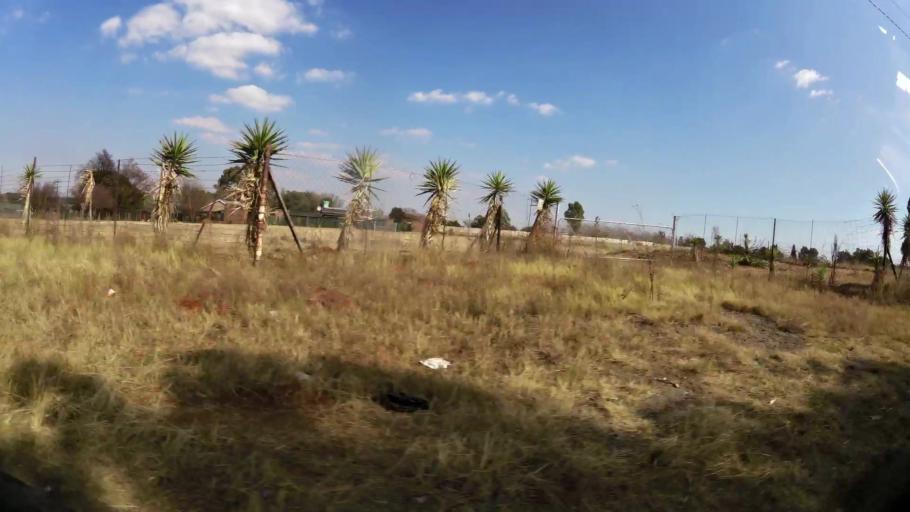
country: ZA
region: Gauteng
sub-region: Ekurhuleni Metropolitan Municipality
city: Benoni
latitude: -26.0873
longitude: 28.3565
